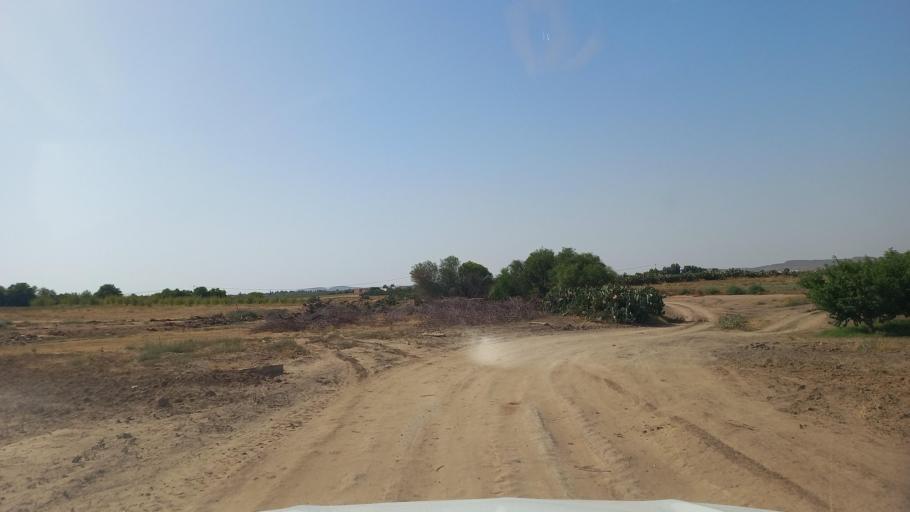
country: TN
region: Al Qasrayn
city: Kasserine
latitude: 35.2525
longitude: 9.0437
